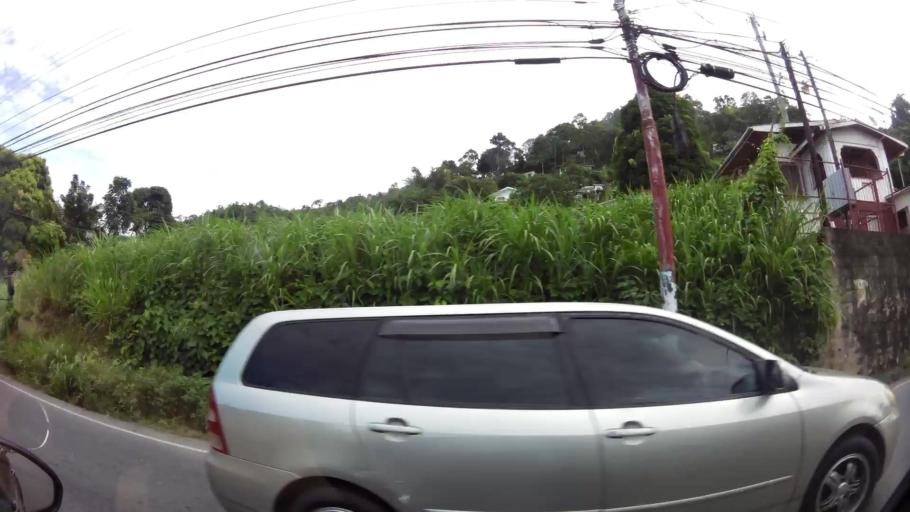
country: TT
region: San Juan/Laventille
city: Laventille
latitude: 10.6639
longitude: -61.4485
